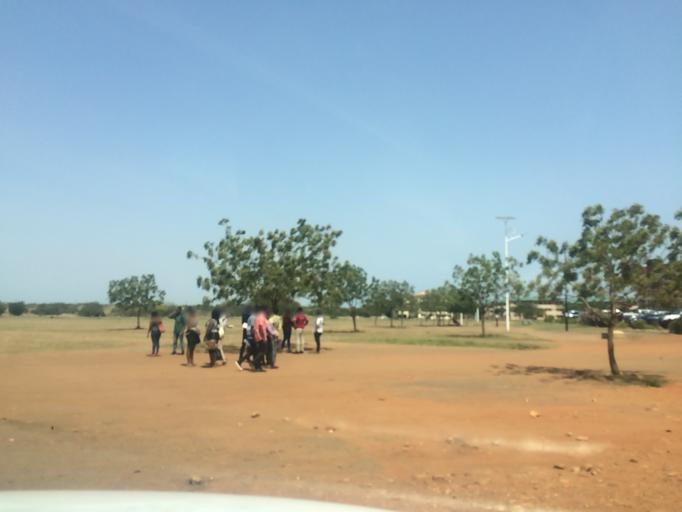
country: GH
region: Greater Accra
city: Tema
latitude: 5.7694
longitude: 0.0831
